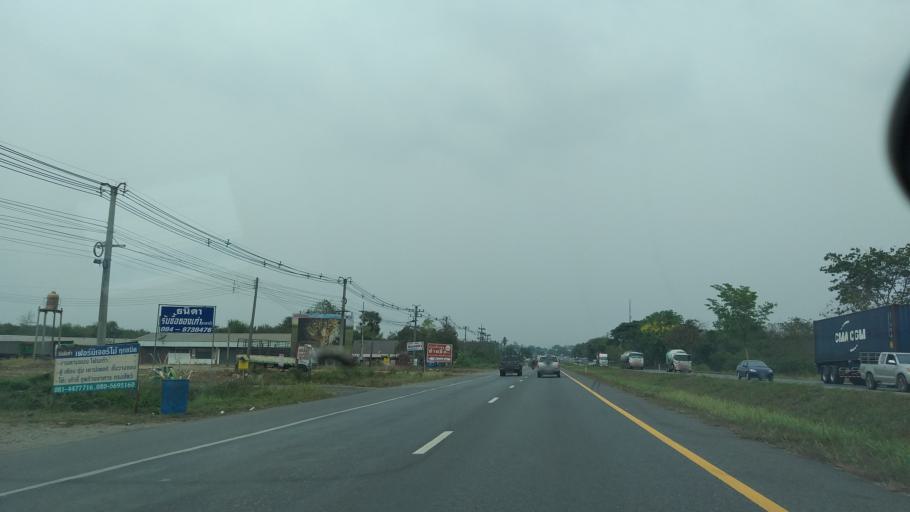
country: TH
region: Chon Buri
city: Ko Chan
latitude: 13.3110
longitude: 101.2656
